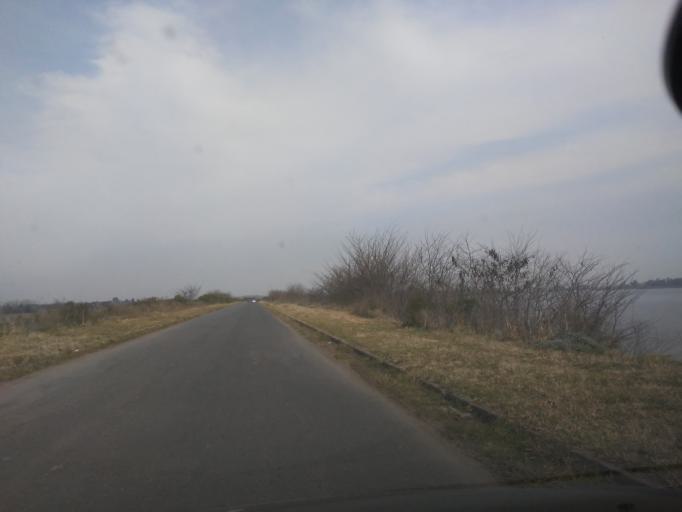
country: AR
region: Buenos Aires
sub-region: Partido de Marcos Paz
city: Marcos Paz
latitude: -34.6797
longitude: -58.8604
